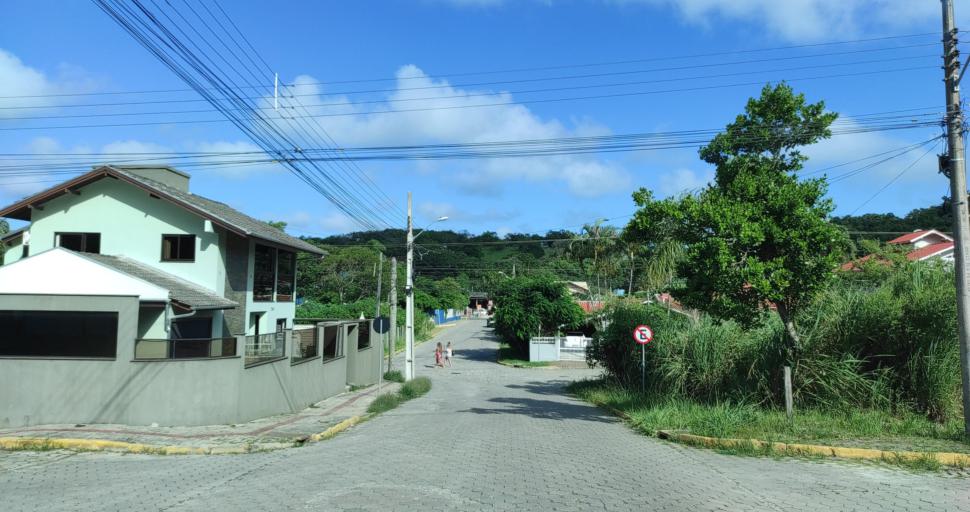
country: BR
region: Santa Catarina
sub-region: Porto Belo
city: Porto Belo
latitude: -27.1554
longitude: -48.4915
